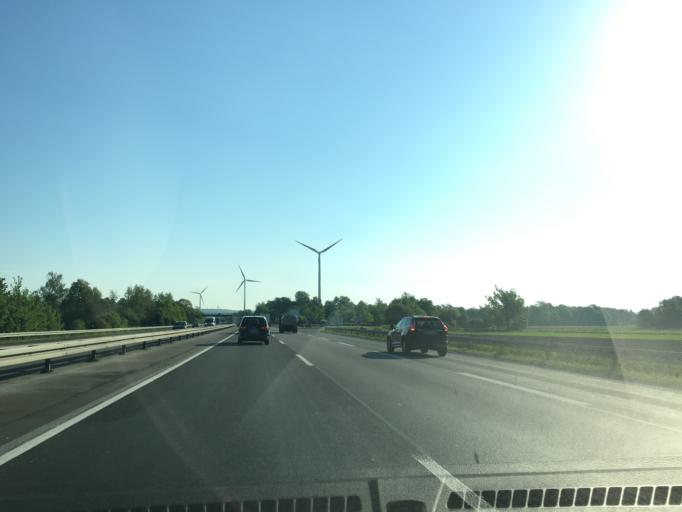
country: DE
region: North Rhine-Westphalia
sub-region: Regierungsbezirk Munster
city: Ladbergen
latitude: 52.1786
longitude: 7.7781
